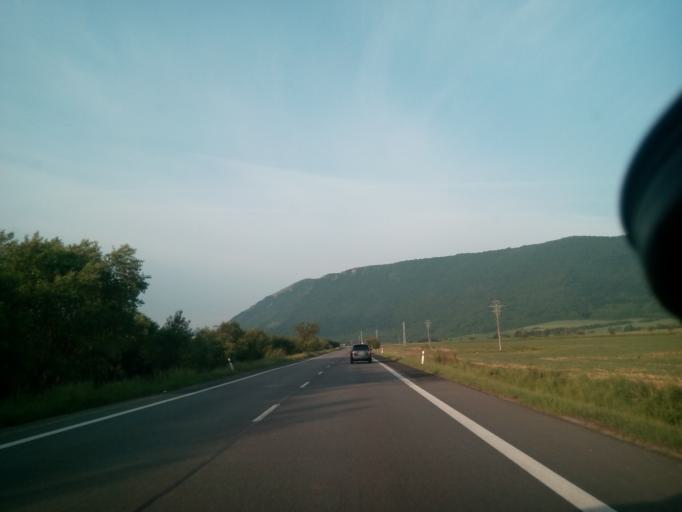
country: SK
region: Kosicky
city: Roznava
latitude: 48.6214
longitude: 20.4938
